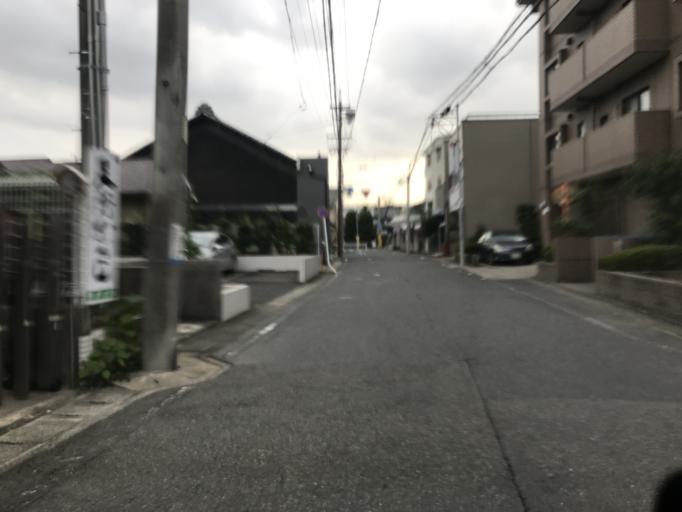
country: JP
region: Aichi
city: Inazawa
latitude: 35.2160
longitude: 136.8388
